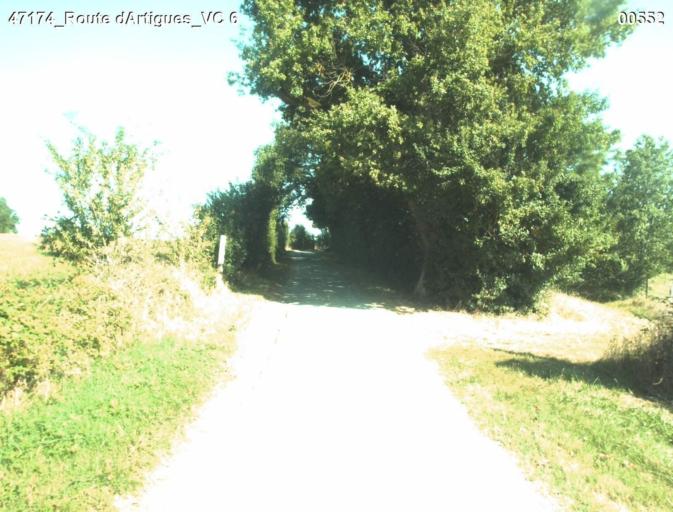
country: FR
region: Midi-Pyrenees
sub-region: Departement du Gers
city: Condom
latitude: 44.0132
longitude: 0.3298
